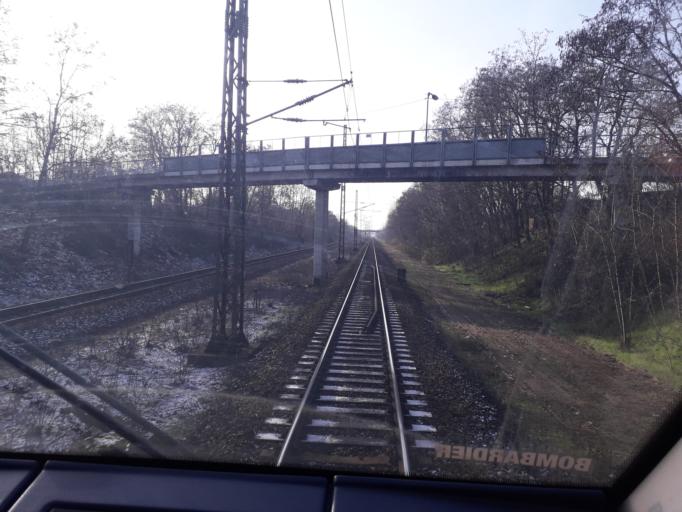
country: DE
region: Berlin
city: Altglienicke
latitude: 52.4035
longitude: 13.5384
